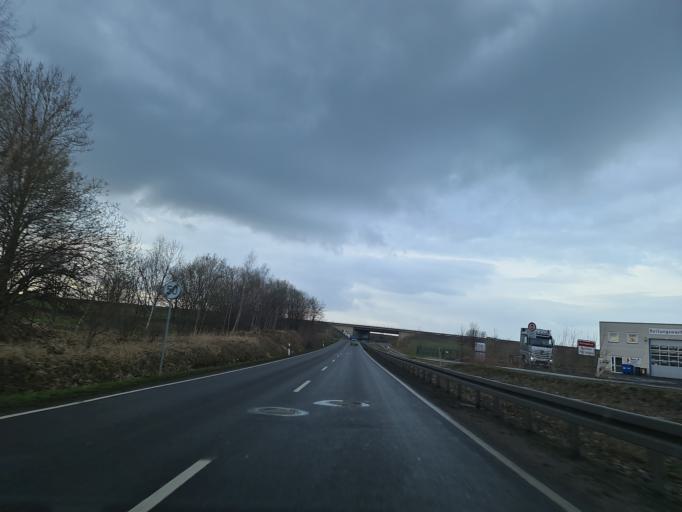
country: DE
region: Saxony
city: Reinsdorf
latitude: 50.6816
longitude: 12.5914
